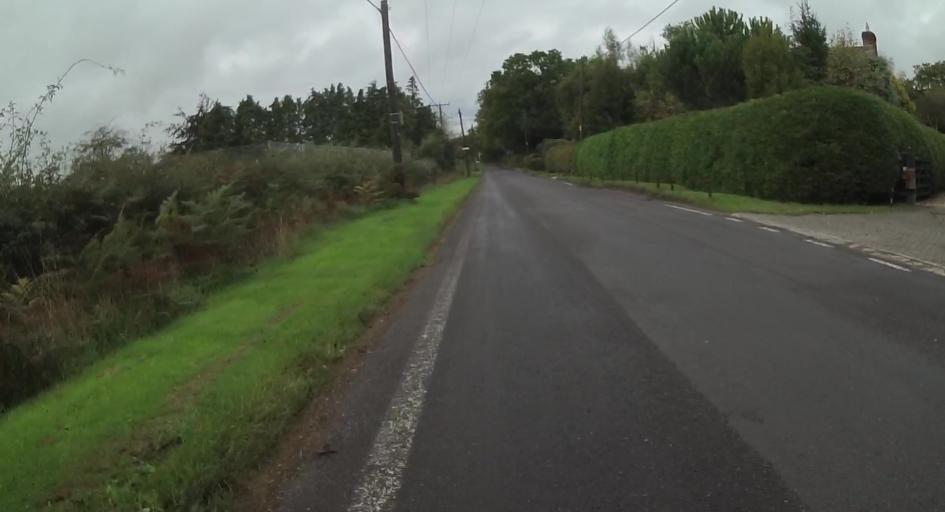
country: GB
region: England
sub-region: Hampshire
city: Tadley
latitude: 51.3157
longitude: -1.1603
